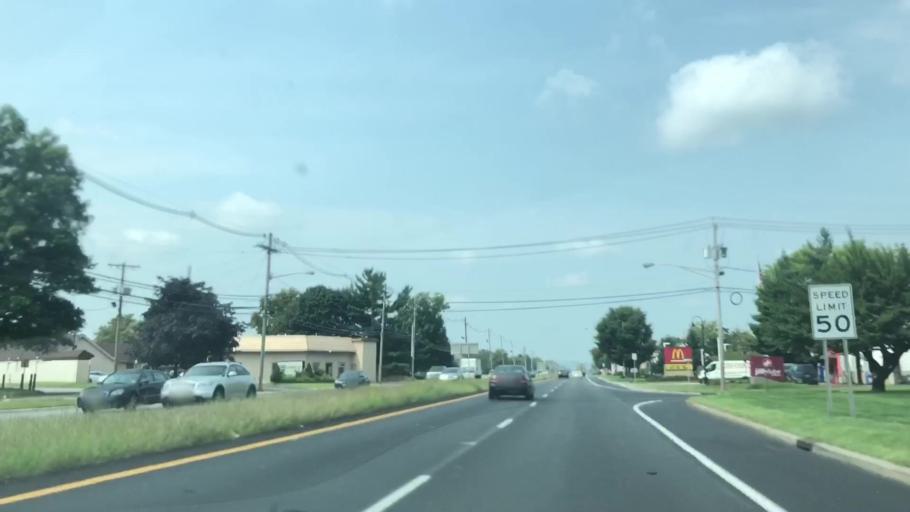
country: US
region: New Jersey
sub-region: Essex County
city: West Caldwell
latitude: 40.8591
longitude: -74.3309
